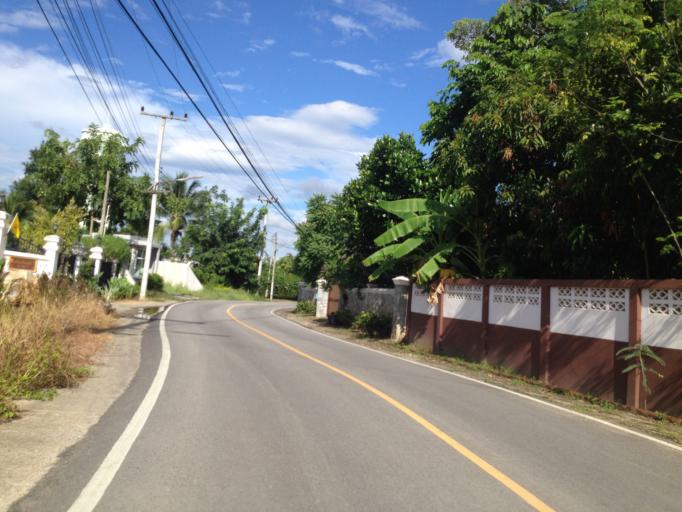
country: TH
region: Chiang Mai
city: Hang Dong
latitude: 18.6848
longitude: 98.9110
